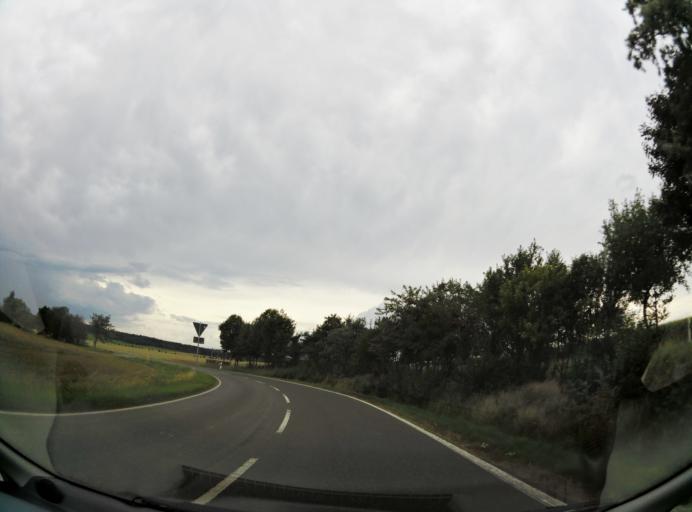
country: DE
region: Thuringia
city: Tanna
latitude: 50.5314
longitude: 11.8724
